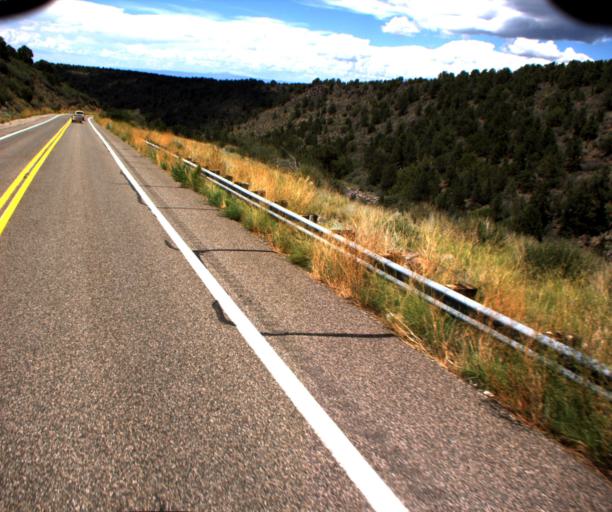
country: US
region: Arizona
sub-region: Yavapai County
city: Lake Montezuma
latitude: 34.5022
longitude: -111.6416
